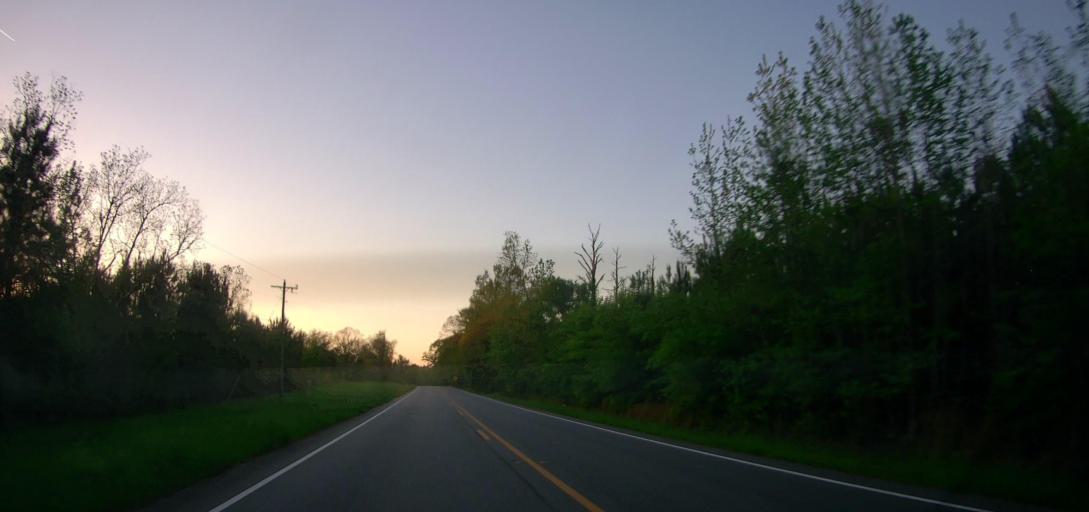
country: US
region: Georgia
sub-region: Marion County
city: Buena Vista
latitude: 32.3507
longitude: -84.5344
